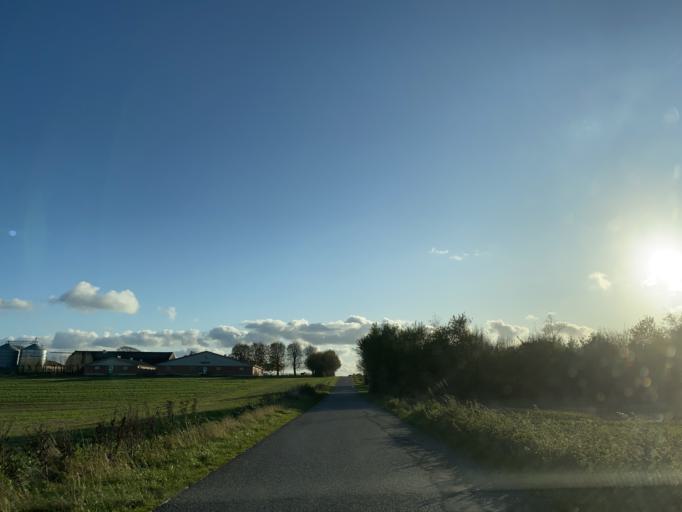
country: DK
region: Central Jutland
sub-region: Viborg Kommune
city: Bjerringbro
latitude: 56.3360
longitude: 9.7107
